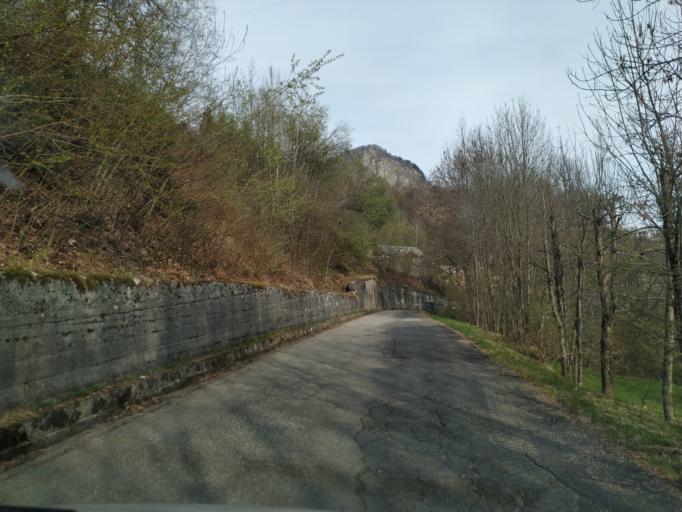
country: IT
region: Piedmont
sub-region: Provincia di Vercelli
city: Piode
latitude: 45.7686
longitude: 8.0501
